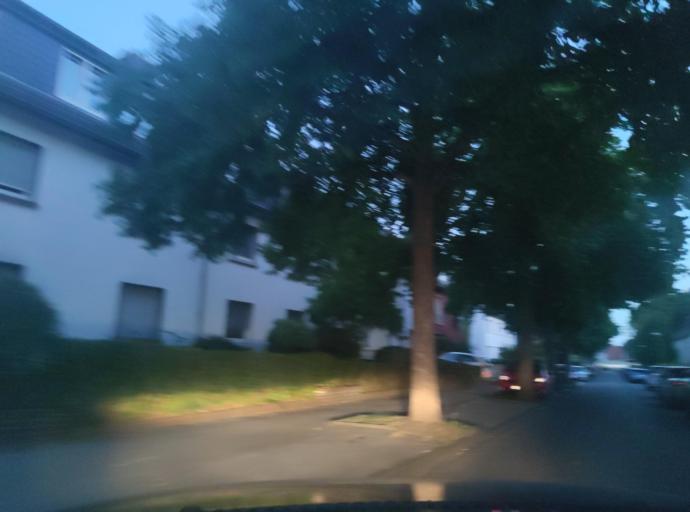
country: DE
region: North Rhine-Westphalia
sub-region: Regierungsbezirk Dusseldorf
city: Essen
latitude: 51.4579
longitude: 7.0455
